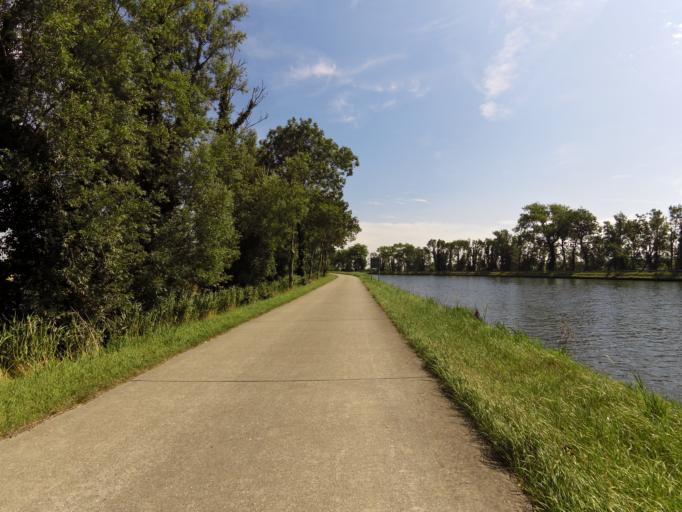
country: BE
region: Flanders
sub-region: Provincie West-Vlaanderen
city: Oudenburg
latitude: 51.2095
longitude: 3.0067
